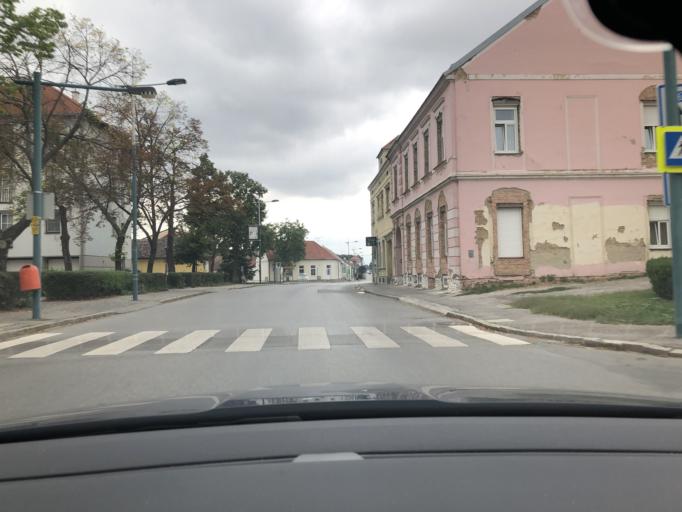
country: AT
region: Lower Austria
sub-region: Politischer Bezirk Mistelbach
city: Laa an der Thaya
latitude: 48.7251
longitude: 16.3839
